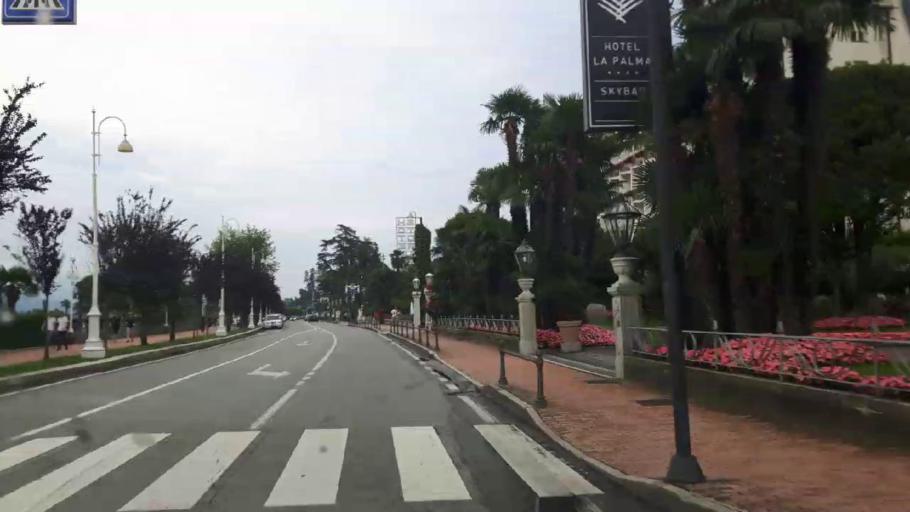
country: IT
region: Piedmont
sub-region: Provincia Verbano-Cusio-Ossola
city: Stresa
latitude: 45.8857
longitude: 8.5357
